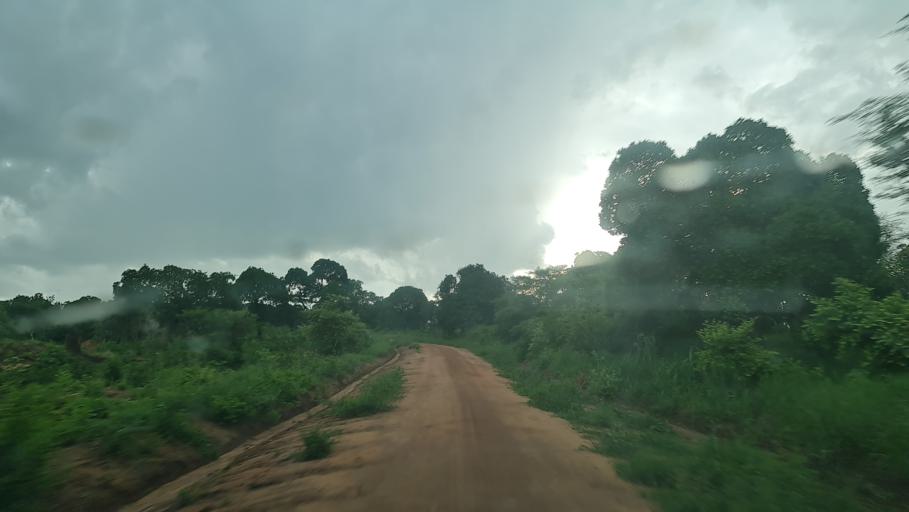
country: MZ
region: Nampula
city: Nacala
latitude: -14.0002
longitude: 40.3599
